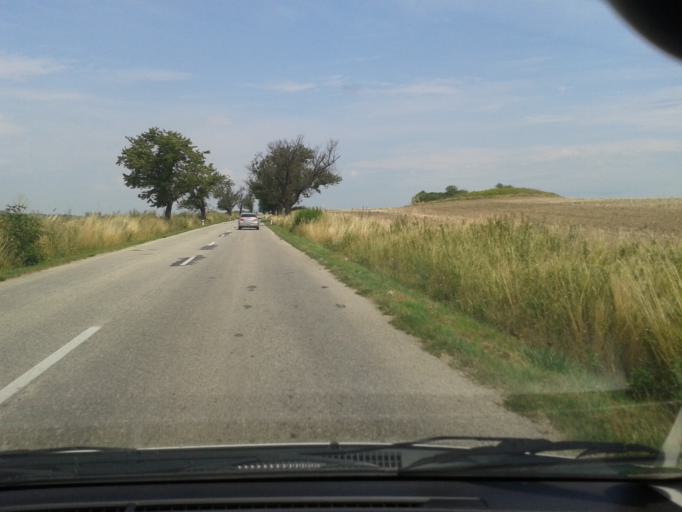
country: HU
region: Komarom-Esztergom
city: Esztergom
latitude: 47.9045
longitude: 18.7550
